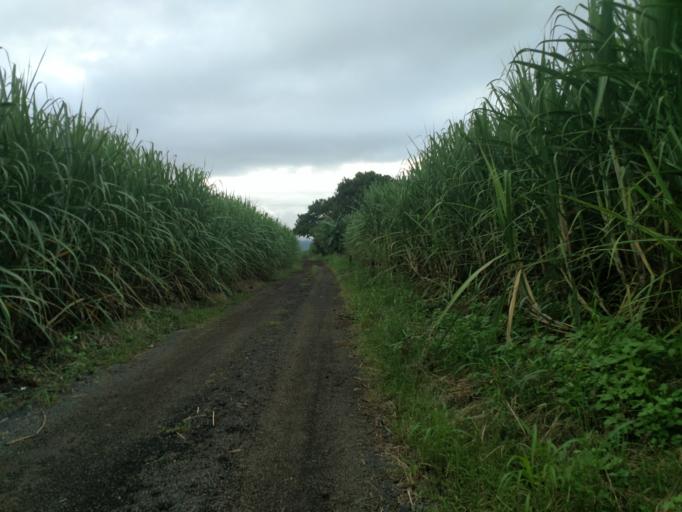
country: MX
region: Nayarit
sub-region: Tepic
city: La Corregidora
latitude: 21.4699
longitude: -104.8017
